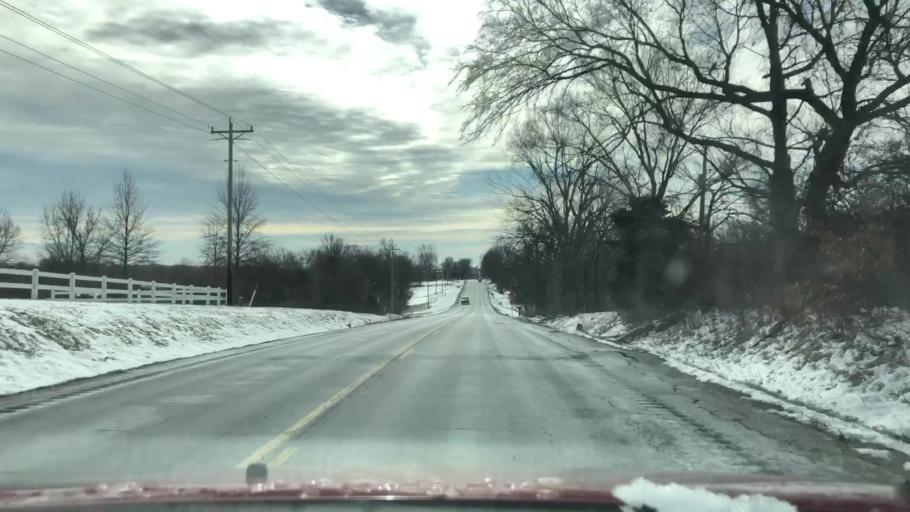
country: US
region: Missouri
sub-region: Jackson County
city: Lone Jack
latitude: 38.8773
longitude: -94.1352
